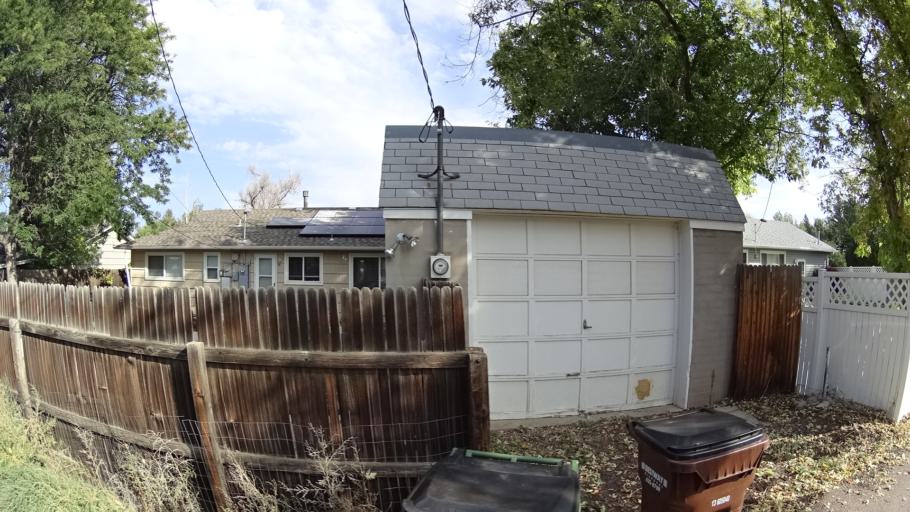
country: US
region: Colorado
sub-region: El Paso County
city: Colorado Springs
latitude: 38.8547
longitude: -104.7806
